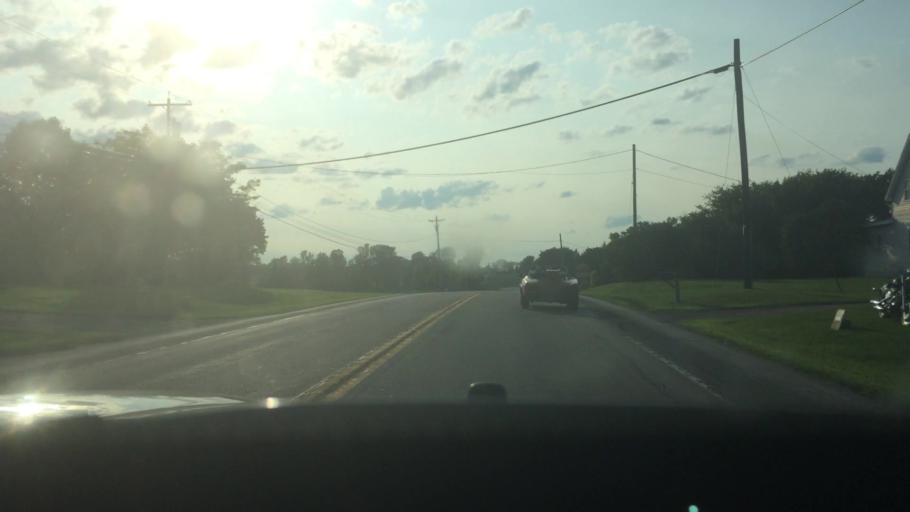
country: US
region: New York
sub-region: St. Lawrence County
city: Ogdensburg
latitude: 44.6680
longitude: -75.3736
